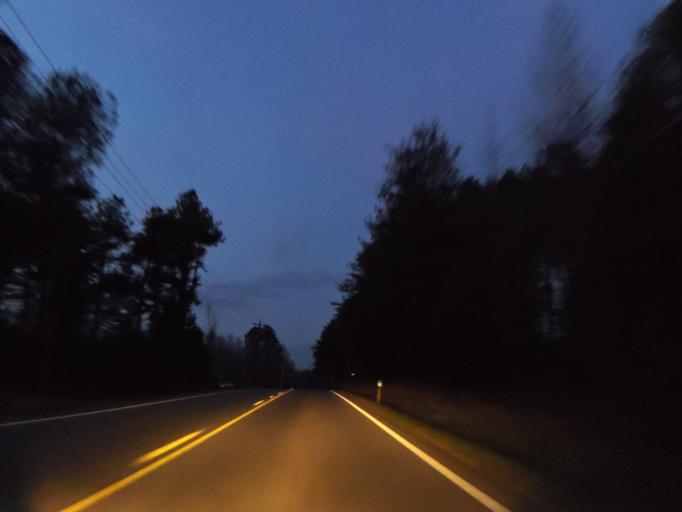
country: US
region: Tennessee
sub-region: Polk County
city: Benton
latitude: 35.1017
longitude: -84.7280
